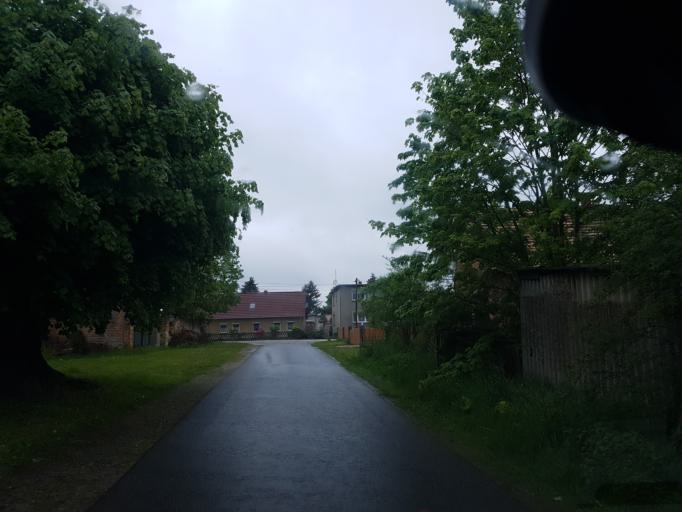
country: DE
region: Brandenburg
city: Tschernitz
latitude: 51.6400
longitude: 14.6042
